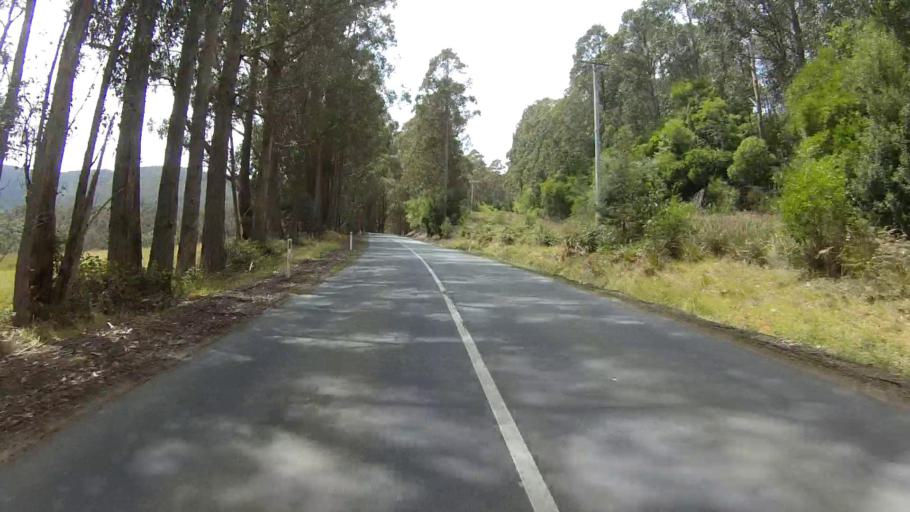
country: AU
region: Tasmania
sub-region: Kingborough
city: Kettering
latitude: -43.1289
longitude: 147.1633
